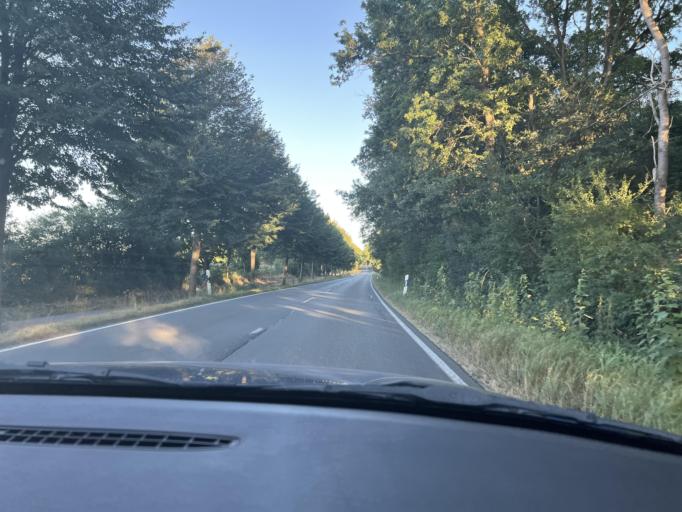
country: DE
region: Schleswig-Holstein
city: Fedderingen
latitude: 54.2909
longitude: 9.1407
